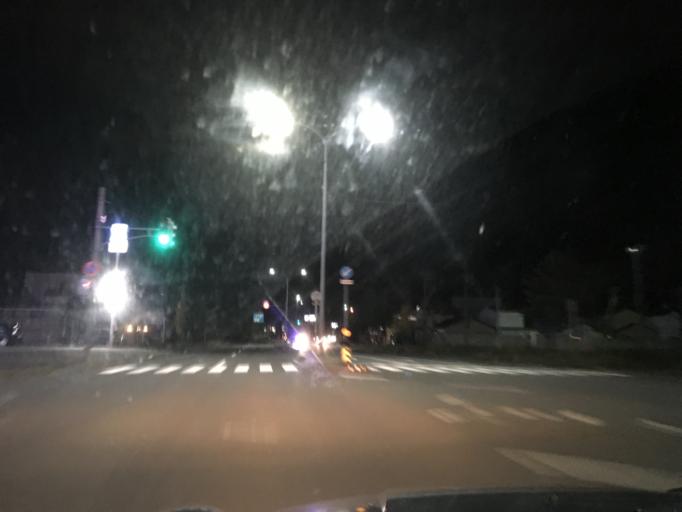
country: JP
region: Hokkaido
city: Muroran
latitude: 42.3596
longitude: 140.9851
